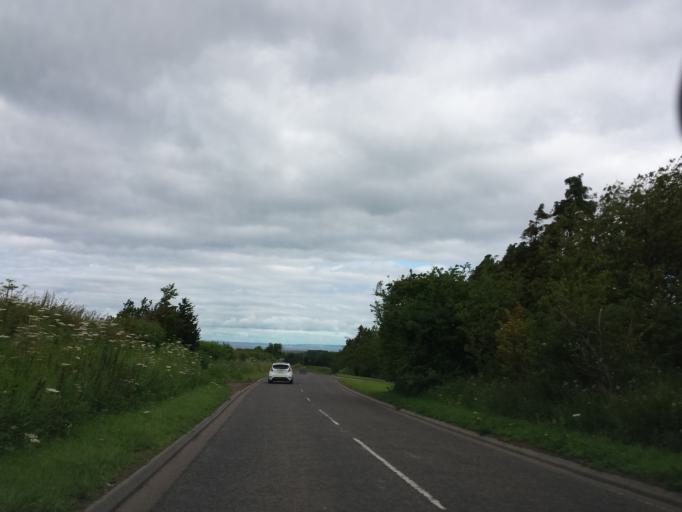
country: GB
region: Scotland
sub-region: East Lothian
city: Gullane
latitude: 55.9856
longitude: -2.8262
